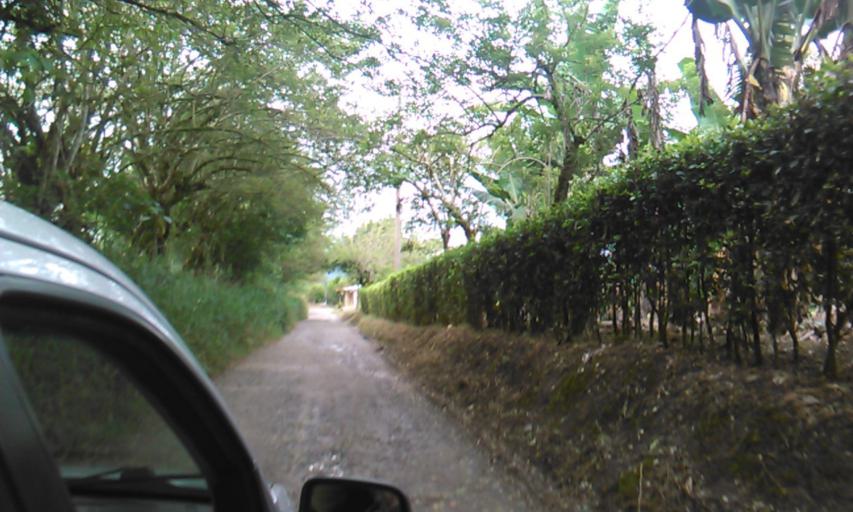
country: CO
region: Quindio
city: La Tebaida
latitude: 4.5128
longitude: -75.8529
